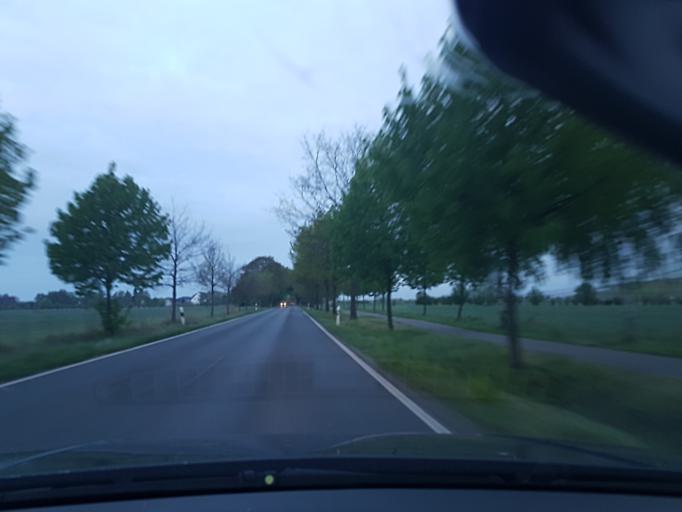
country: DE
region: Berlin
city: Gropiusstadt
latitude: 52.4081
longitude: 13.4723
